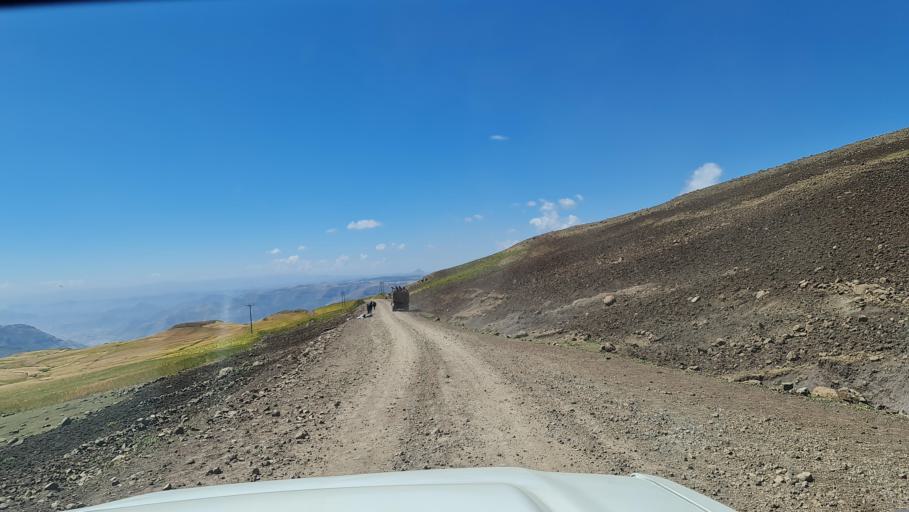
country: ET
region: Amhara
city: Debark'
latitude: 13.2364
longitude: 38.1096
